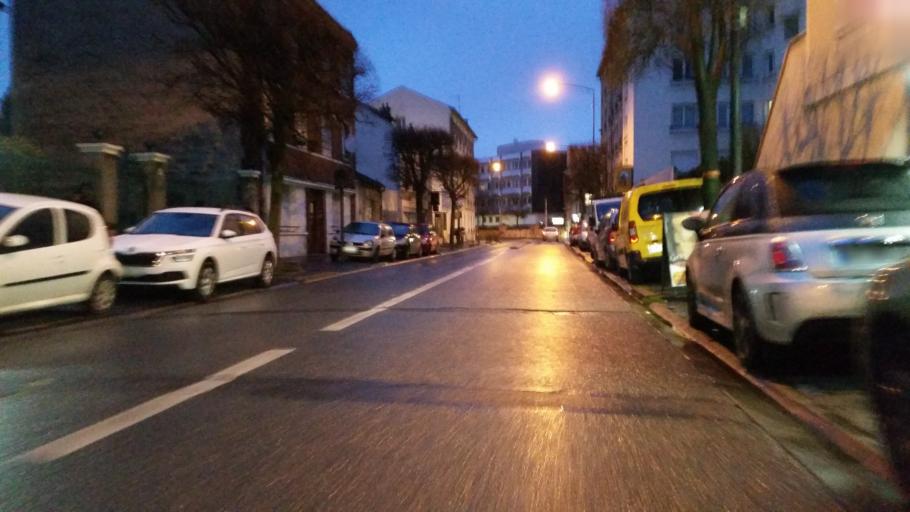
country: FR
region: Ile-de-France
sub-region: Departement du Val-de-Marne
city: Alfortville
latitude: 48.8039
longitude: 2.4047
